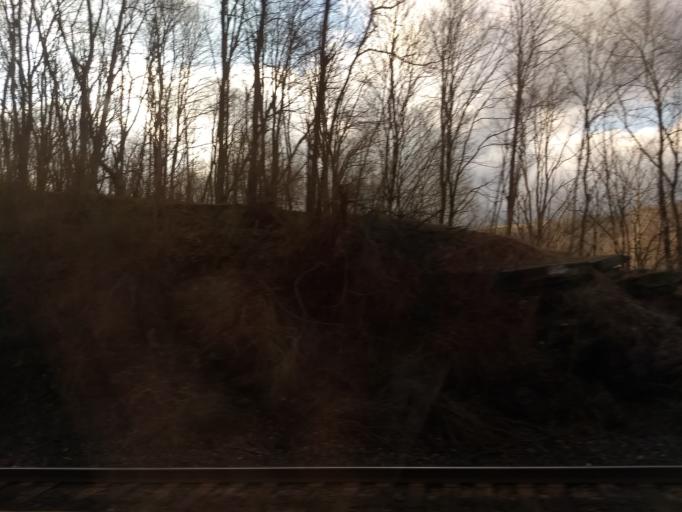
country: US
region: Pennsylvania
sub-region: Cambria County
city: Beaverdale
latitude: 40.3777
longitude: -78.7489
